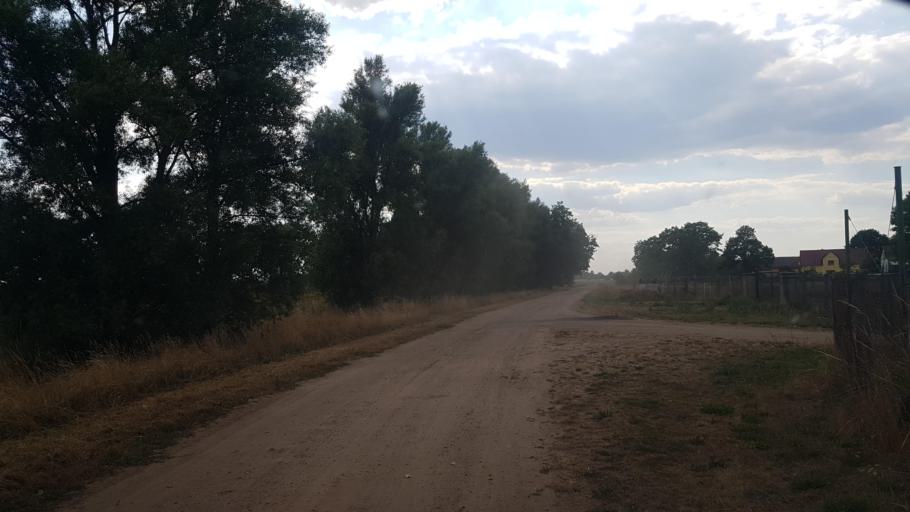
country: DE
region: Brandenburg
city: Herzberg
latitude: 51.6829
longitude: 13.2771
